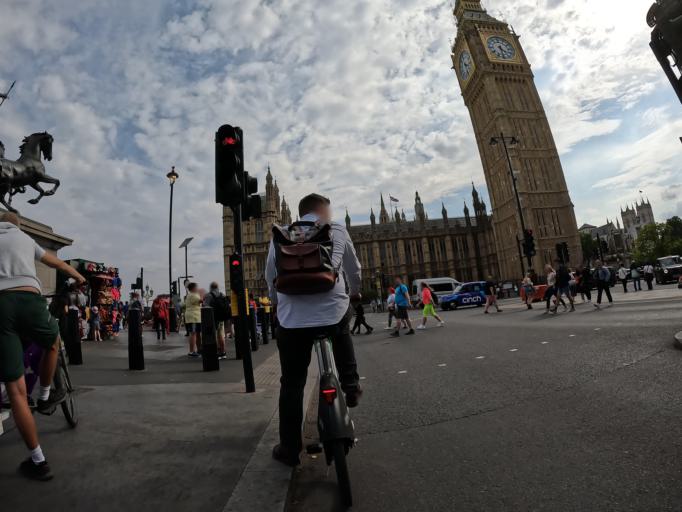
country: GB
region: England
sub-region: Kent
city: Halstead
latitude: 51.3416
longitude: 0.1232
